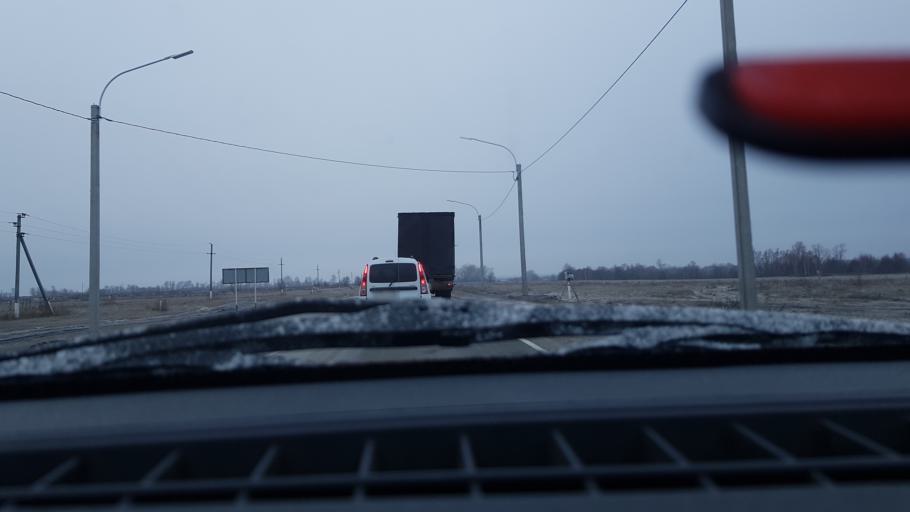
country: RU
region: Ulyanovsk
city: Novaya Mayna
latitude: 54.1645
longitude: 49.7261
